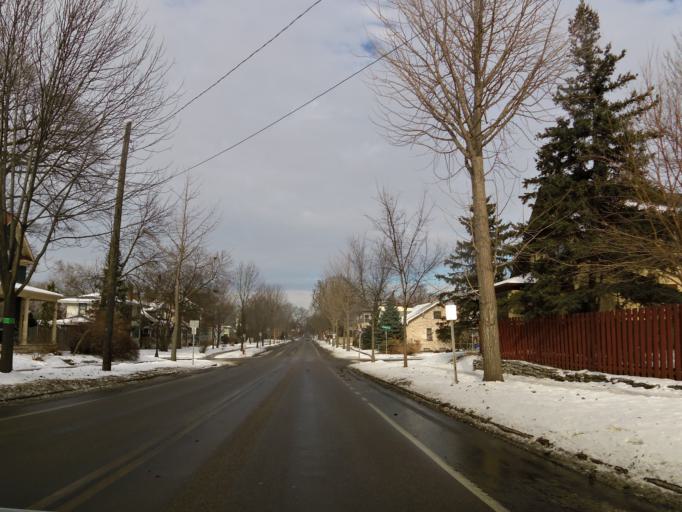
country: US
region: Minnesota
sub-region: Ramsey County
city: Falcon Heights
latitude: 44.9374
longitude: -93.1874
